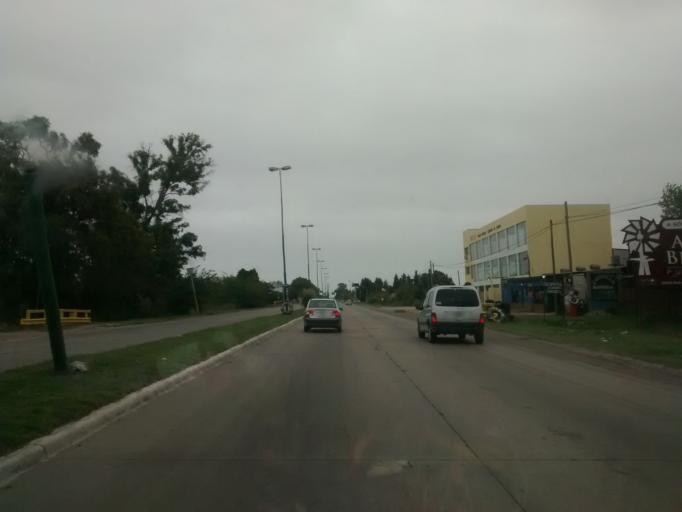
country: AR
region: Buenos Aires
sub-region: Partido de La Plata
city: La Plata
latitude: -35.0035
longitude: -58.0574
